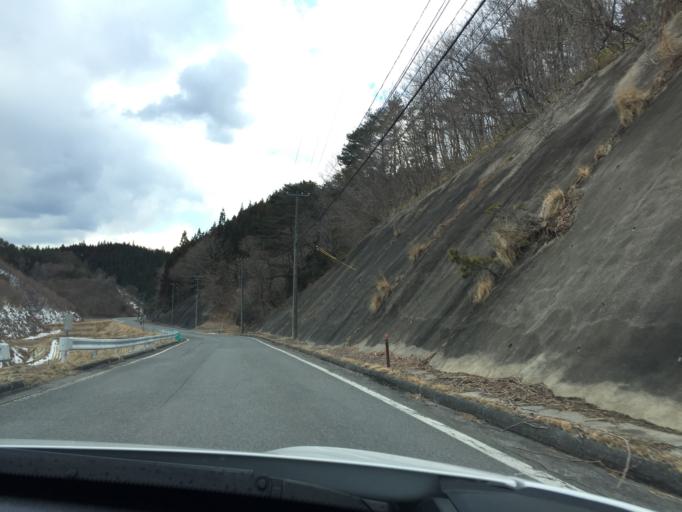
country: JP
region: Fukushima
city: Iwaki
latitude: 37.2331
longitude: 140.7349
